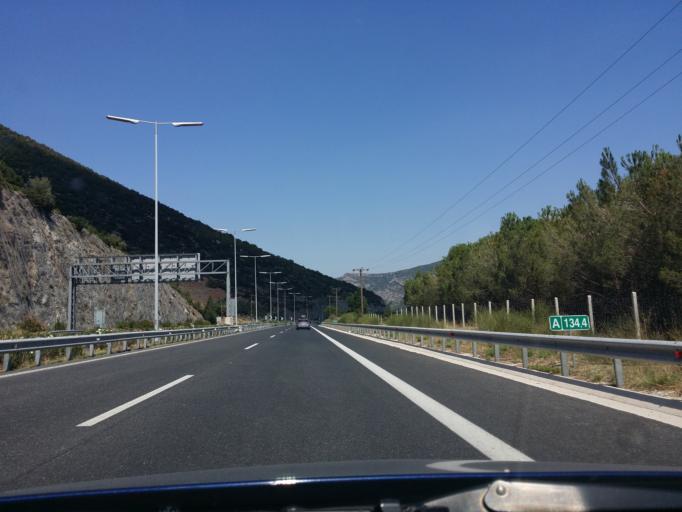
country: GR
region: Peloponnese
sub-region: Nomos Korinthias
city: Nemea
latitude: 37.6855
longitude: 22.5045
